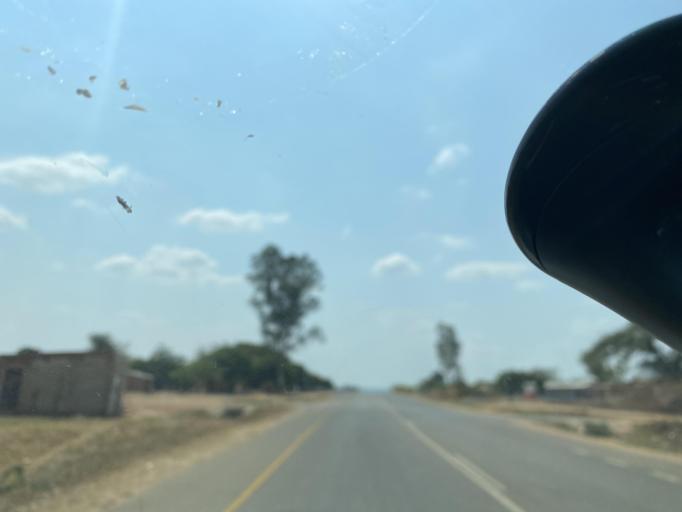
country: ZM
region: Lusaka
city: Chongwe
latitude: -15.5774
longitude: 28.7026
